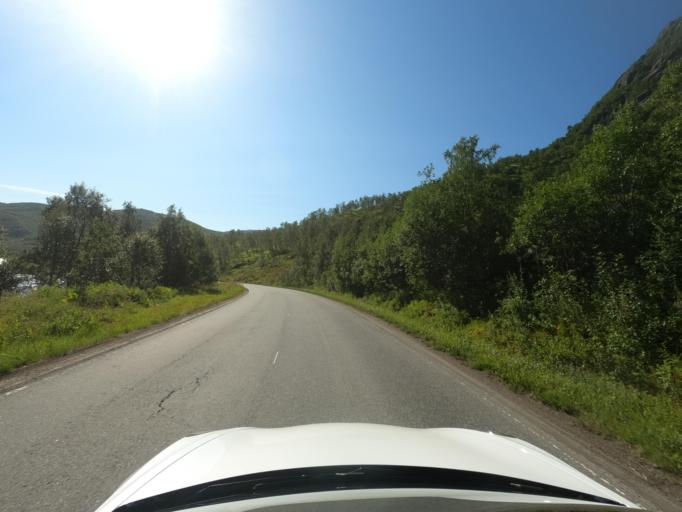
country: NO
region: Nordland
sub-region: Lodingen
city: Lodingen
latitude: 68.5560
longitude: 15.7463
